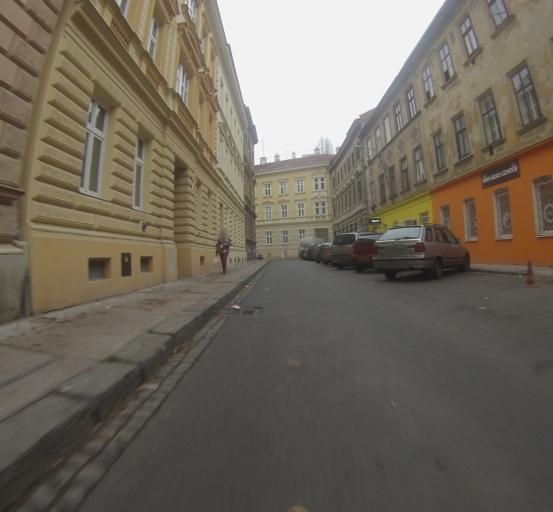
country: CZ
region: South Moravian
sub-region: Mesto Brno
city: Brno
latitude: 49.2026
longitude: 16.6147
